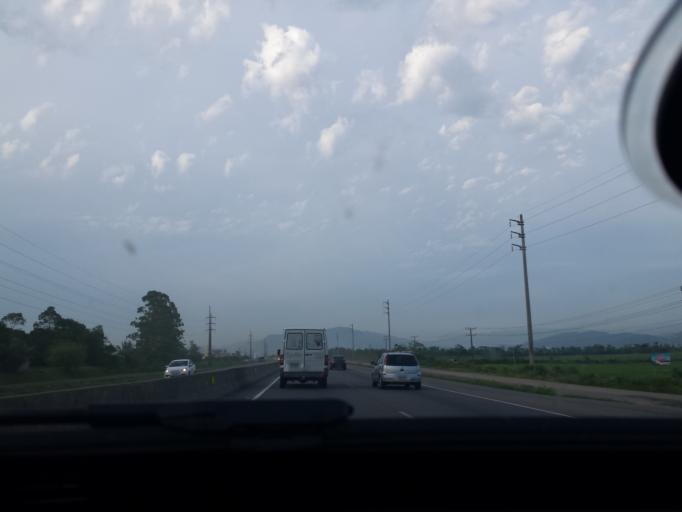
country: BR
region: Santa Catarina
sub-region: Tubarao
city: Tubarao
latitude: -28.4563
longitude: -48.9826
